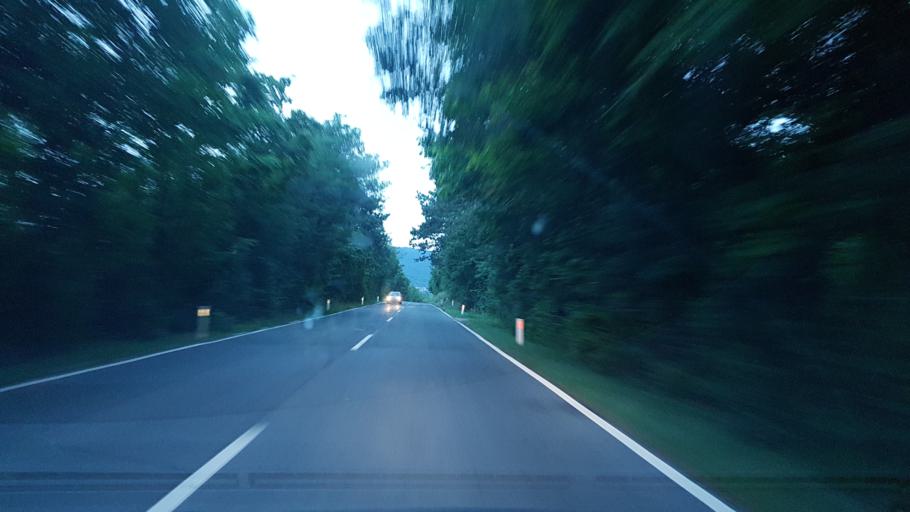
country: SI
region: Divaca
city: Divaca
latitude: 45.6697
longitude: 13.9471
